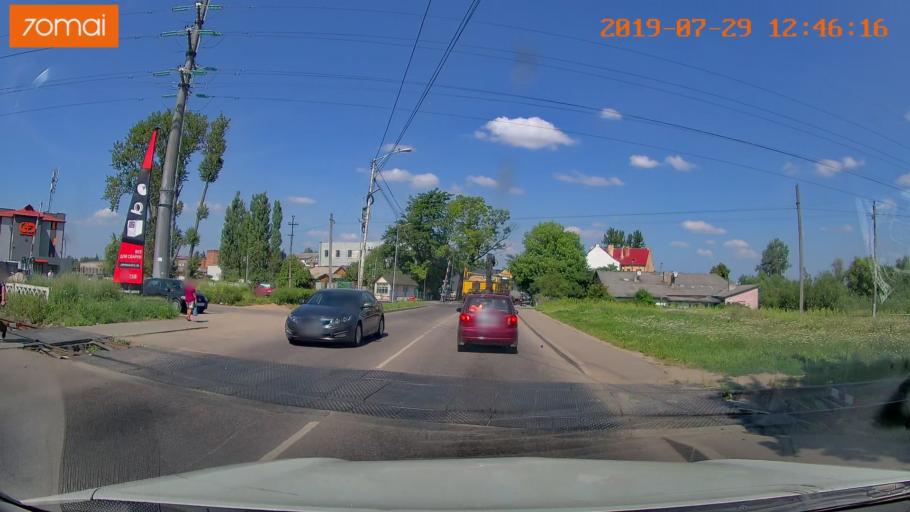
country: RU
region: Kaliningrad
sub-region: Gorod Kaliningrad
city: Kaliningrad
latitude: 54.6818
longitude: 20.5351
